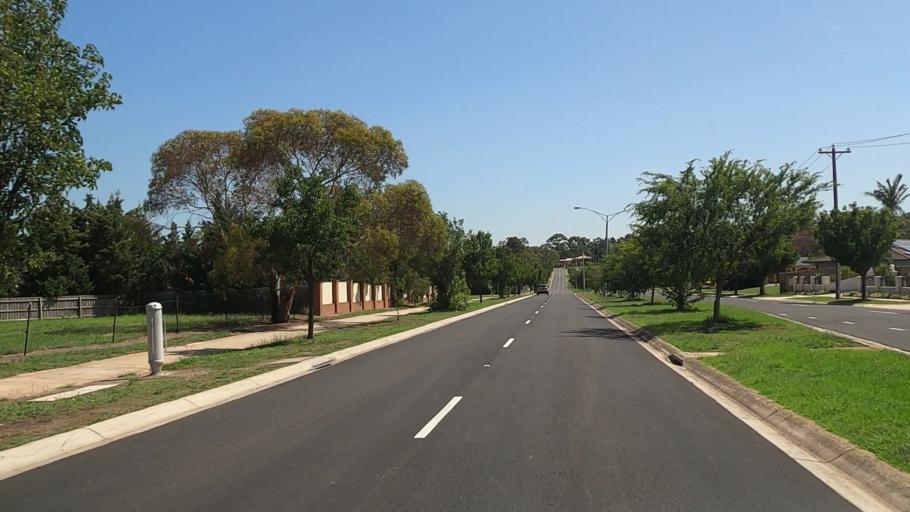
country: AU
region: Victoria
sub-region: Hume
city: Attwood
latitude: -37.6527
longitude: 144.8876
